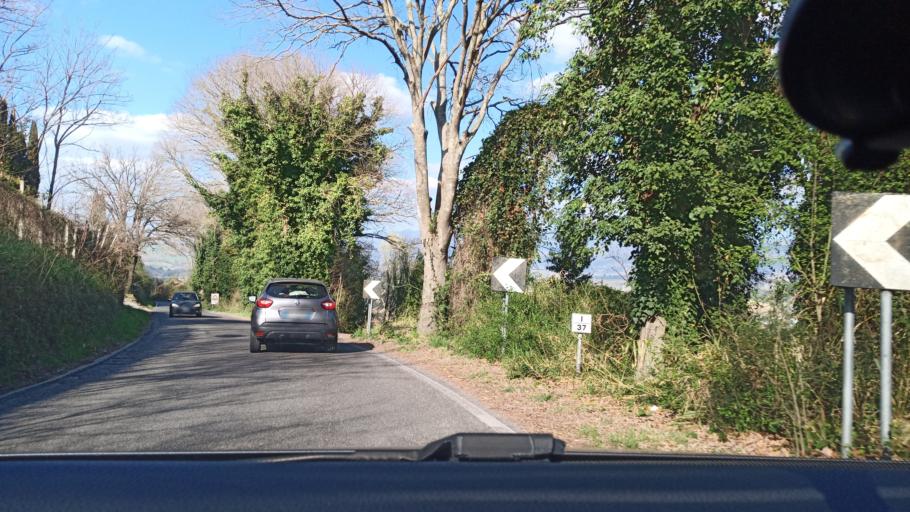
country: IT
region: Latium
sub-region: Citta metropolitana di Roma Capitale
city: Torrita Tiberina
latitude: 42.2431
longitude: 12.6187
